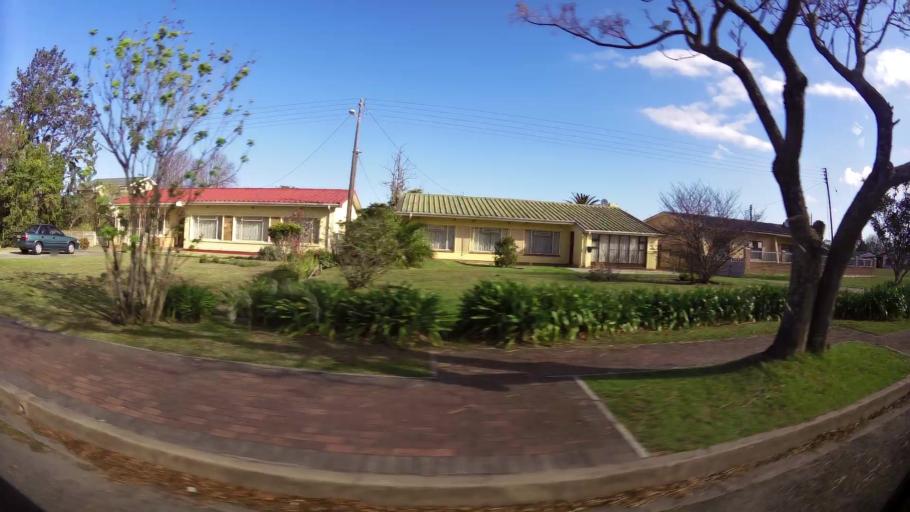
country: ZA
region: Western Cape
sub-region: Eden District Municipality
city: George
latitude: -33.9664
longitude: 22.4792
